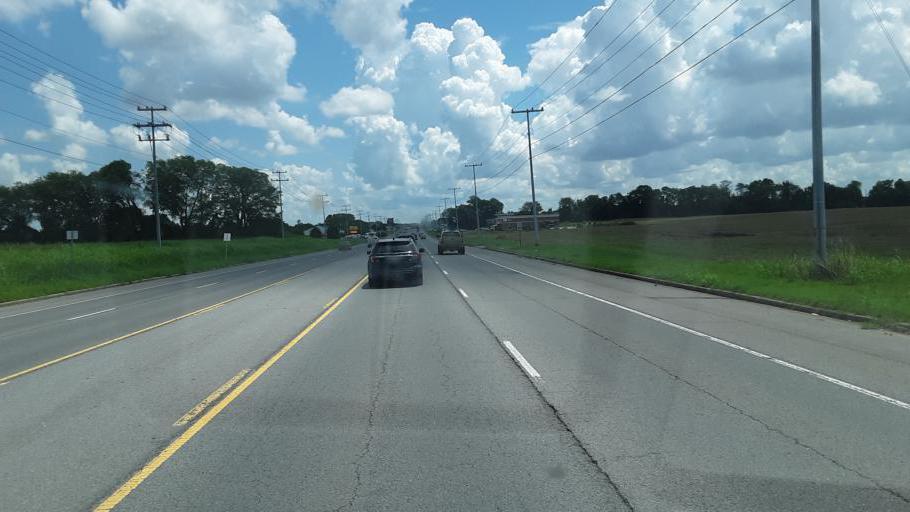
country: US
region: Tennessee
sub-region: Montgomery County
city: Clarksville
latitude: 36.6279
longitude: -87.3378
